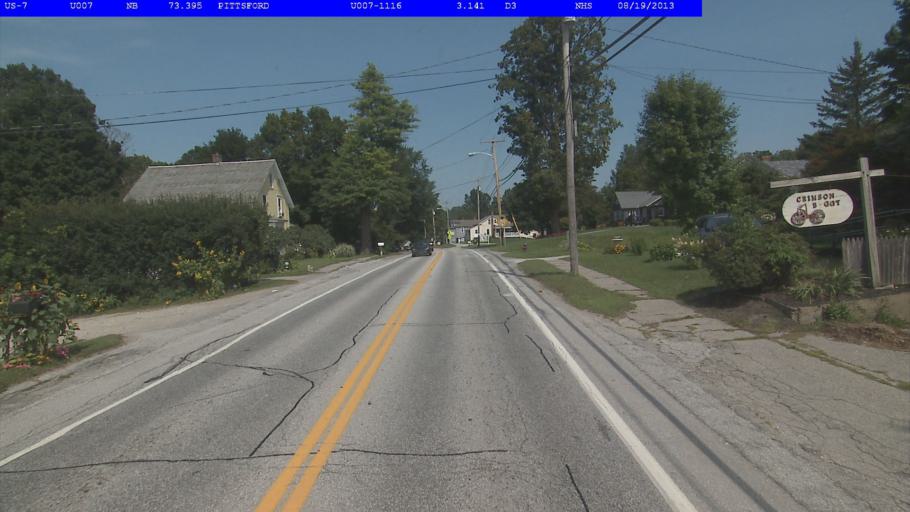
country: US
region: Vermont
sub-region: Rutland County
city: Rutland
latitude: 43.7043
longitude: -73.0132
